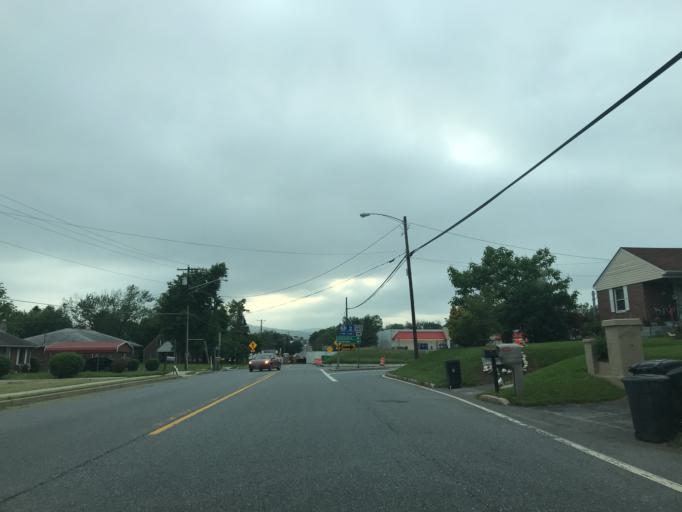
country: US
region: Maryland
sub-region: Frederick County
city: Emmitsburg
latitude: 39.7024
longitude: -77.3162
